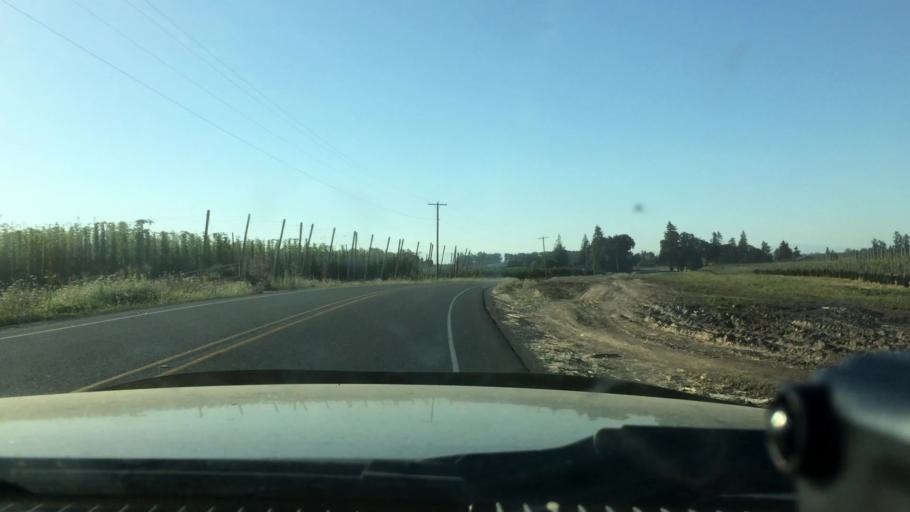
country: US
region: Oregon
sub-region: Marion County
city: Gervais
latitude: 45.1260
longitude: -122.9903
